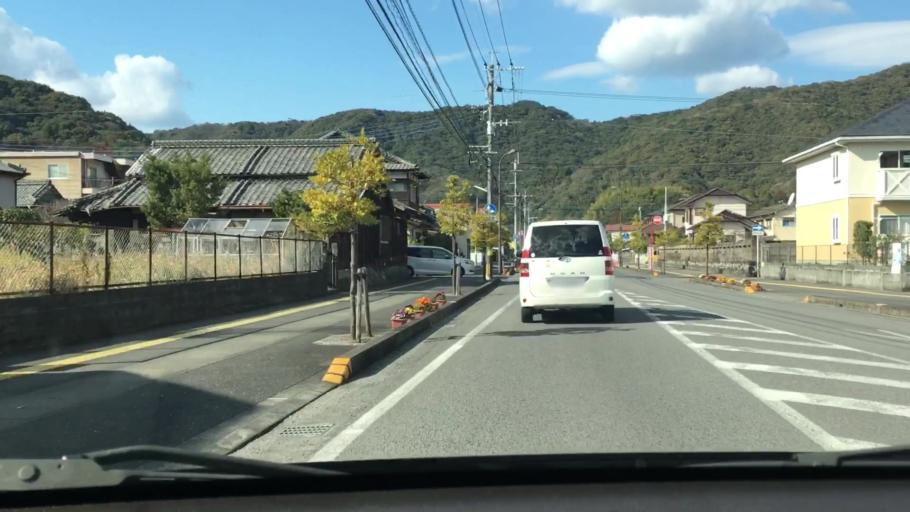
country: JP
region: Oita
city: Saiki
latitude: 32.9621
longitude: 131.8989
